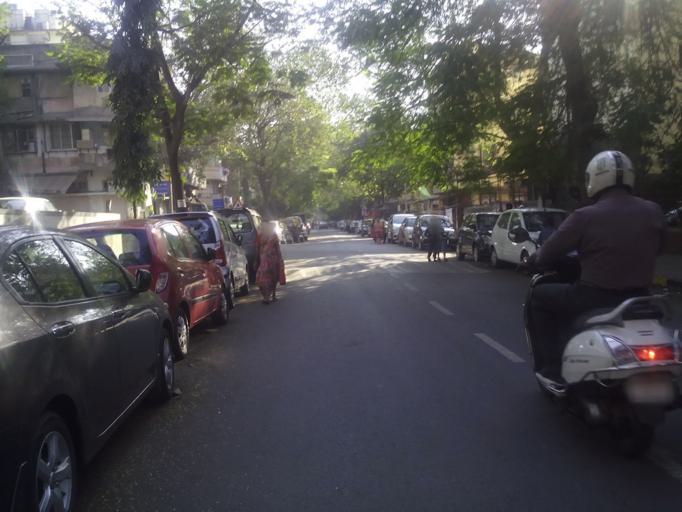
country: IN
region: Maharashtra
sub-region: Mumbai Suburban
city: Mumbai
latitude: 19.0427
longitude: 72.8626
